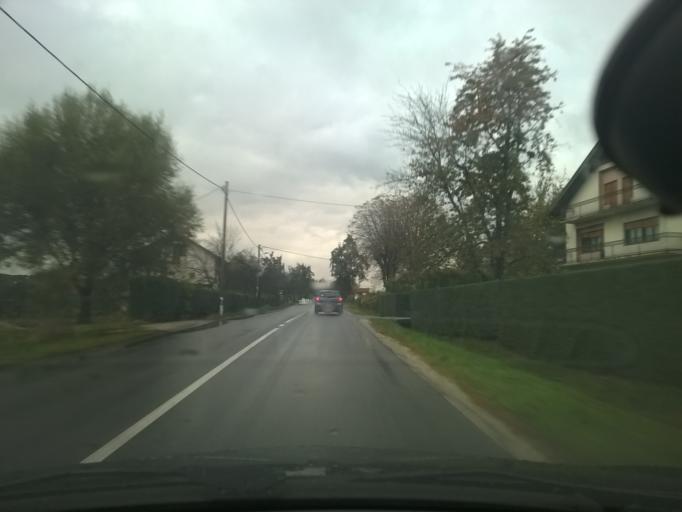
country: HR
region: Krapinsko-Zagorska
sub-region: Grad Krapina
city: Krapina
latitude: 46.1332
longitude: 15.8857
